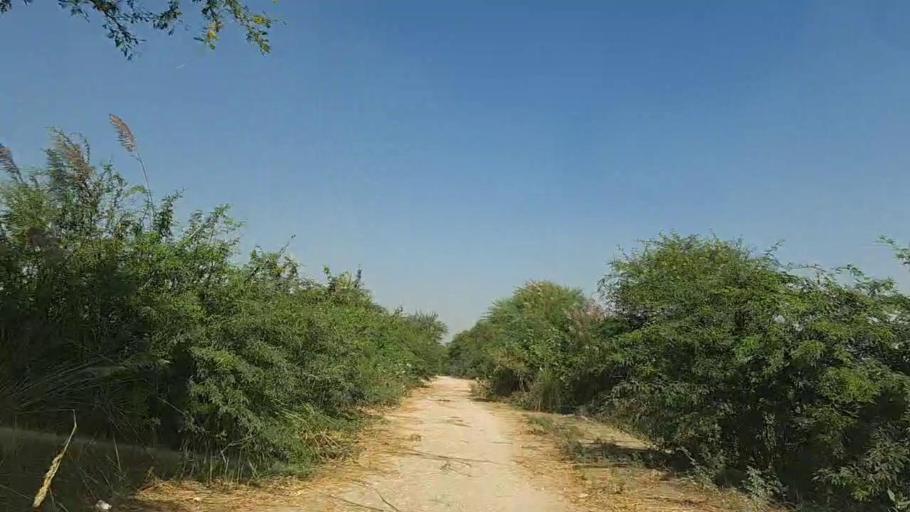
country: PK
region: Sindh
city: Daro Mehar
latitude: 24.8075
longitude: 68.1833
